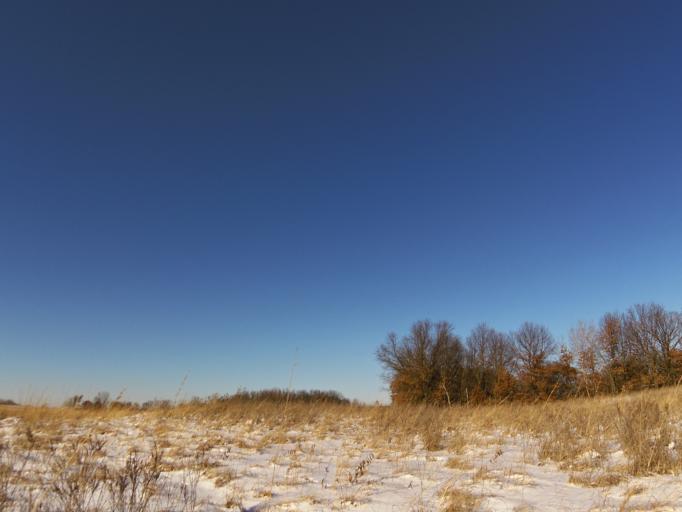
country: US
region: Minnesota
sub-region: Washington County
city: Lake Elmo
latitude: 44.9814
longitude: -92.9086
